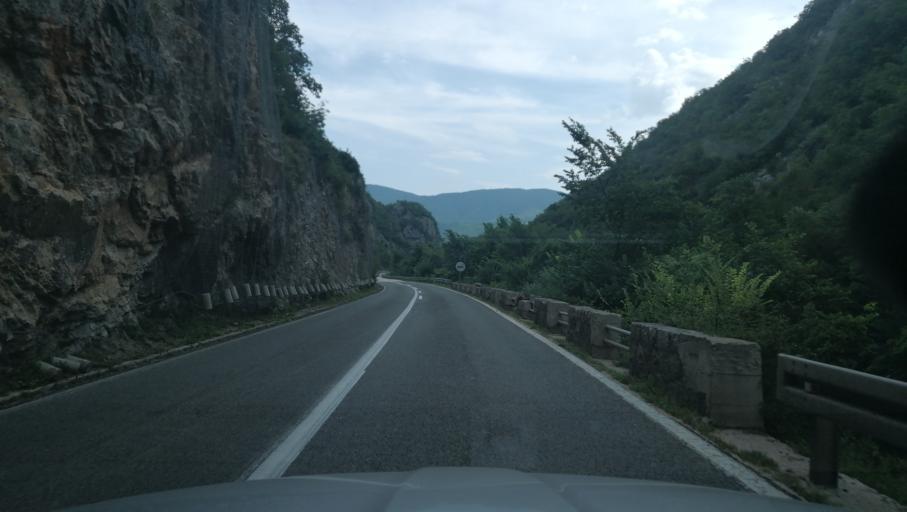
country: BA
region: Republika Srpska
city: Hiseti
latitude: 44.6050
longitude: 17.1373
